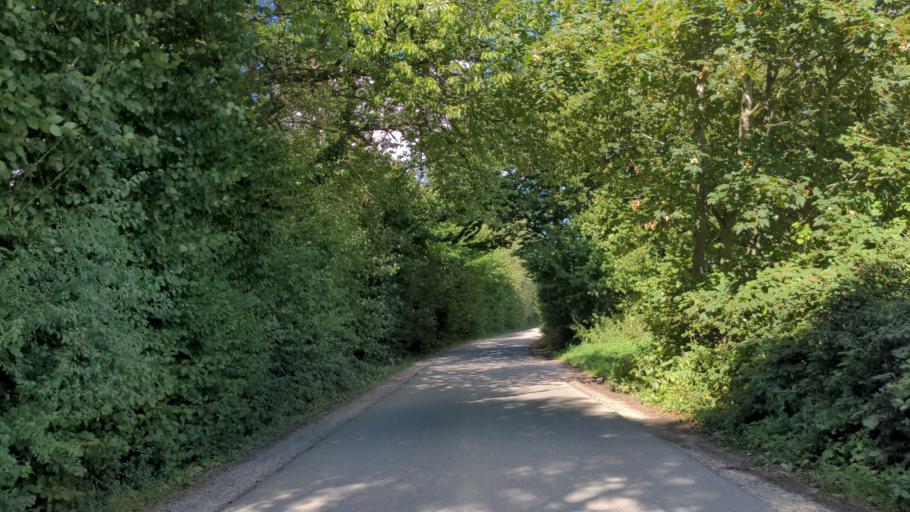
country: DE
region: Schleswig-Holstein
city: Beschendorf
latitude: 54.1830
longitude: 10.8214
